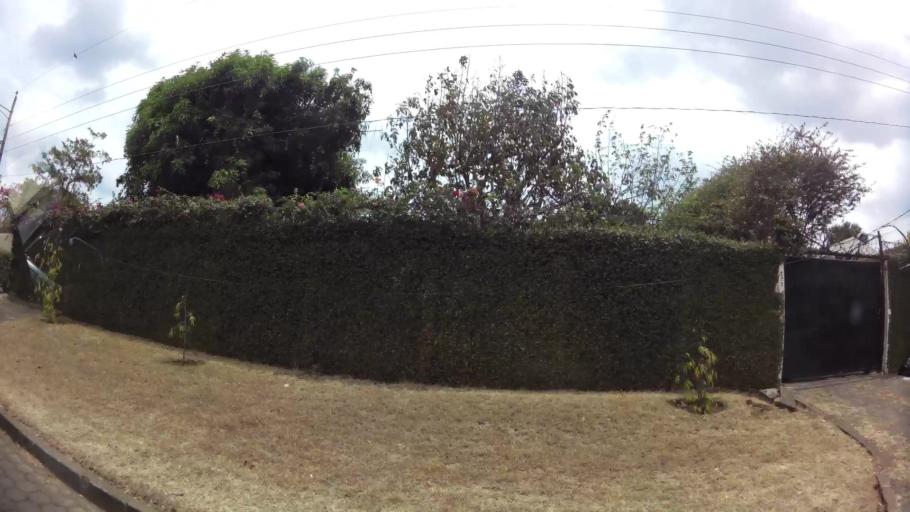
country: NI
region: Managua
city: Managua
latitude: 12.0956
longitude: -86.2292
